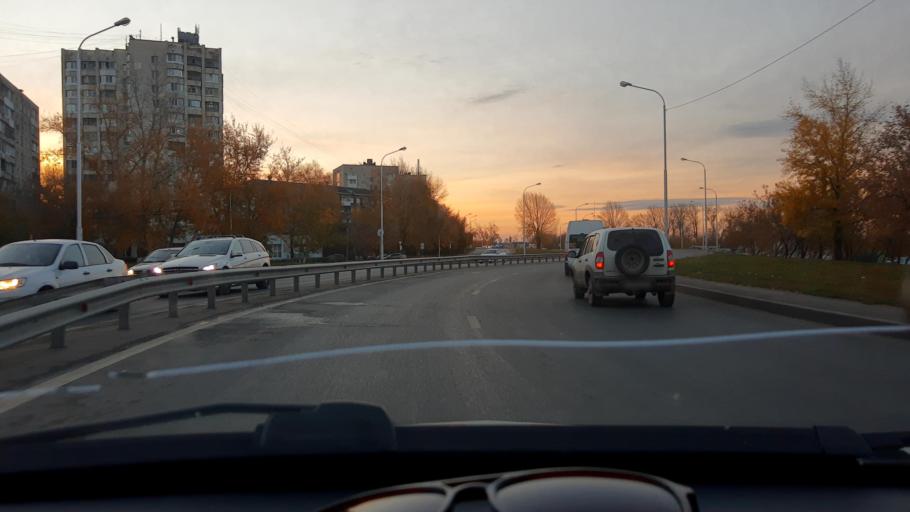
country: RU
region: Bashkortostan
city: Ufa
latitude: 54.8027
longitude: 56.1103
